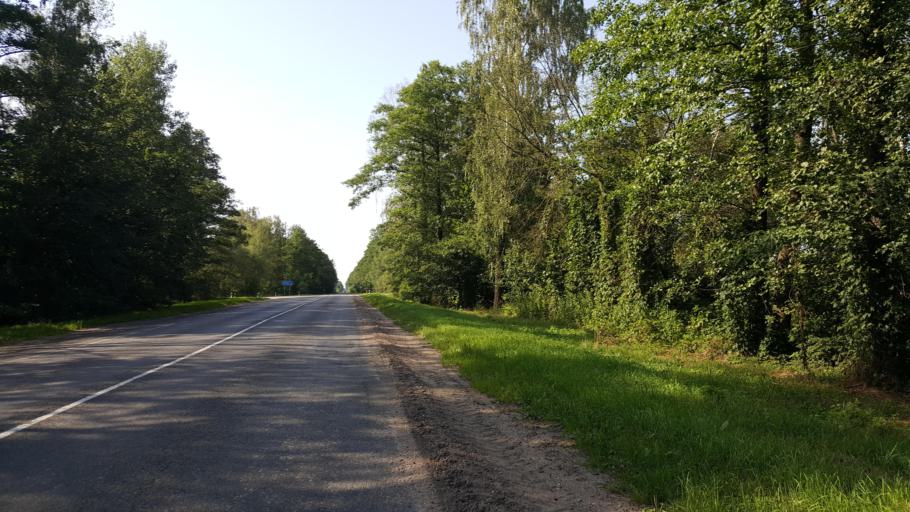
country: BY
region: Brest
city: Zhabinka
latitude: 52.2648
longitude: 23.9598
